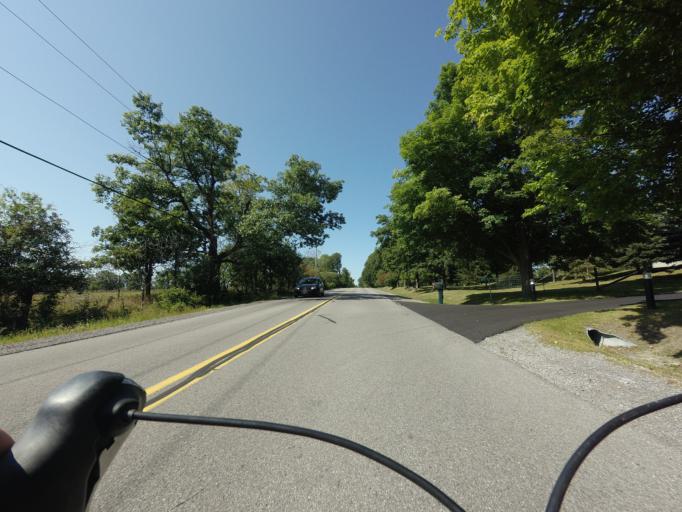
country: CA
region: Ontario
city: Bells Corners
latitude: 45.4089
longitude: -75.9313
